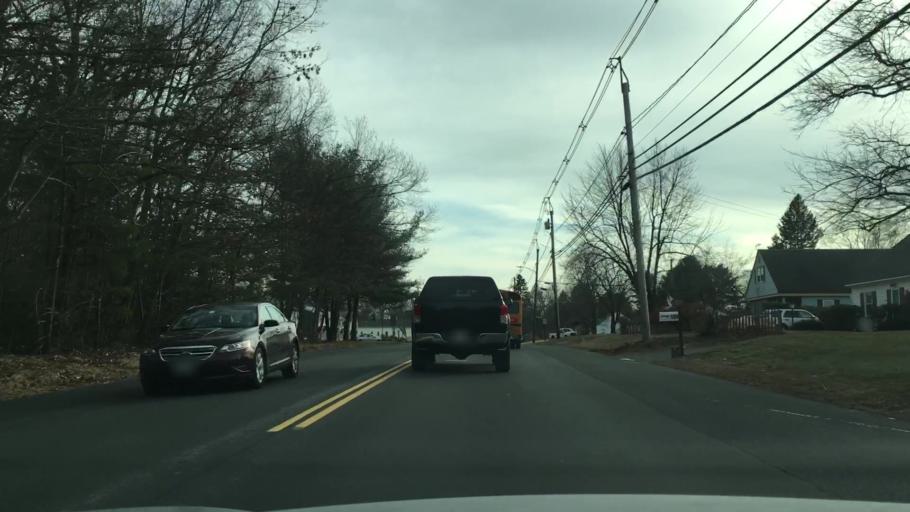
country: US
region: Massachusetts
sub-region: Hampden County
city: Westfield
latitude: 42.1052
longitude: -72.7646
